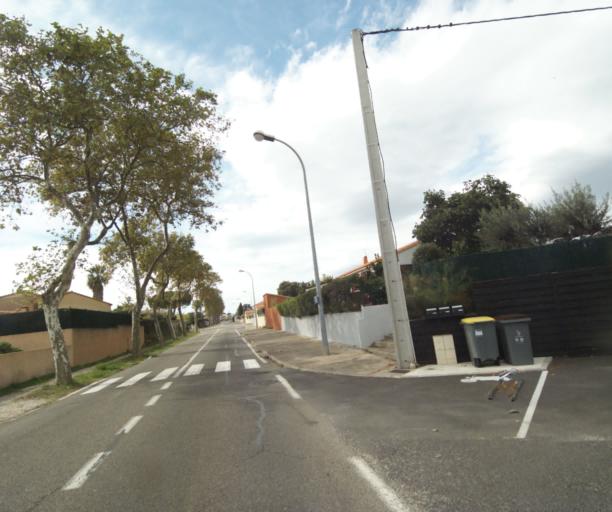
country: FR
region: Languedoc-Roussillon
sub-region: Departement des Pyrenees-Orientales
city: Argelers
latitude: 42.5499
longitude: 3.0178
